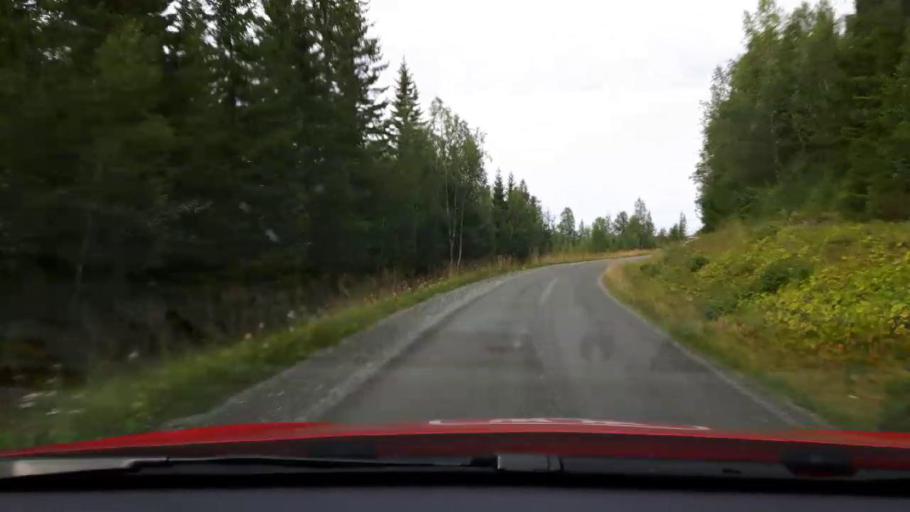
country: SE
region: Jaemtland
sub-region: Are Kommun
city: Are
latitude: 63.7596
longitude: 13.0917
